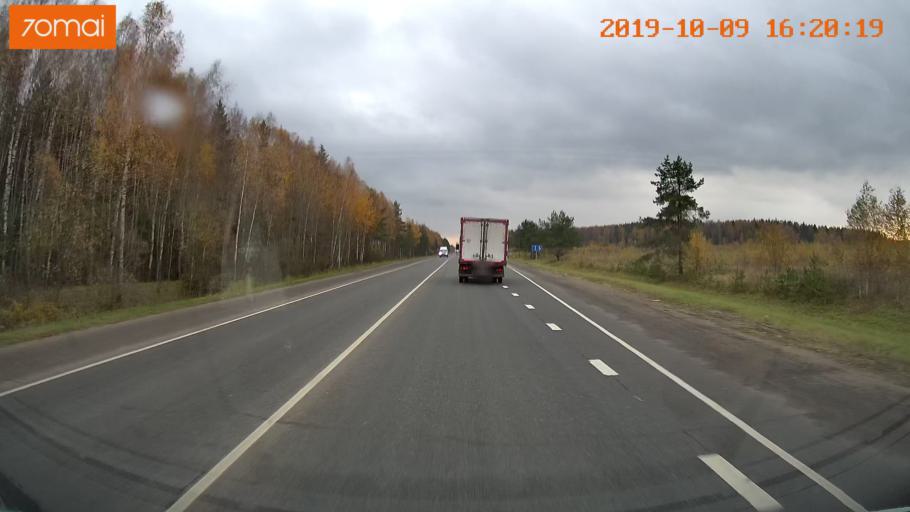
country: RU
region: Kostroma
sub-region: Kostromskoy Rayon
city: Kostroma
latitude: 57.7079
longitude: 40.8924
